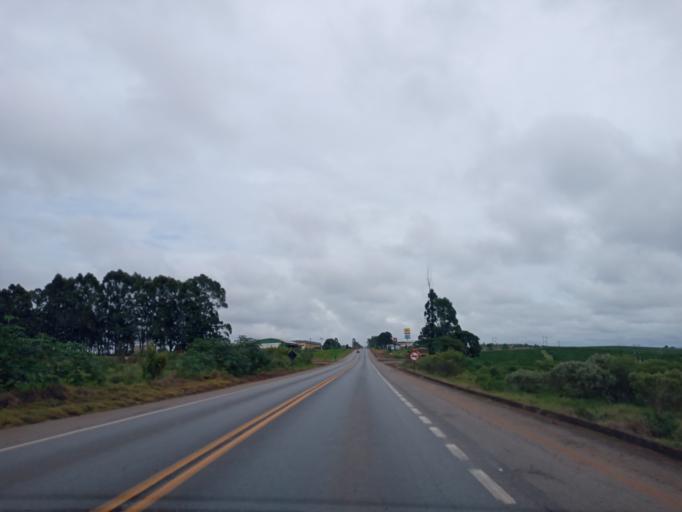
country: BR
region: Minas Gerais
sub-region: Campos Altos
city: Campos Altos
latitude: -19.6600
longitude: -46.2072
